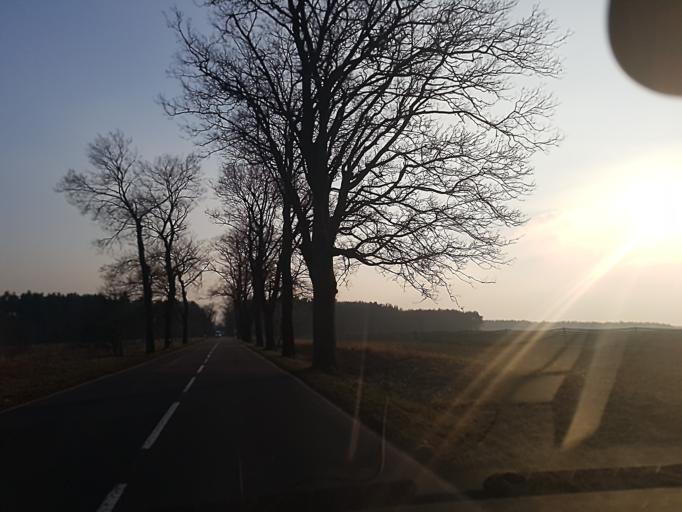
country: DE
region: Saxony-Anhalt
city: Coswig
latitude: 51.9931
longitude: 12.4719
